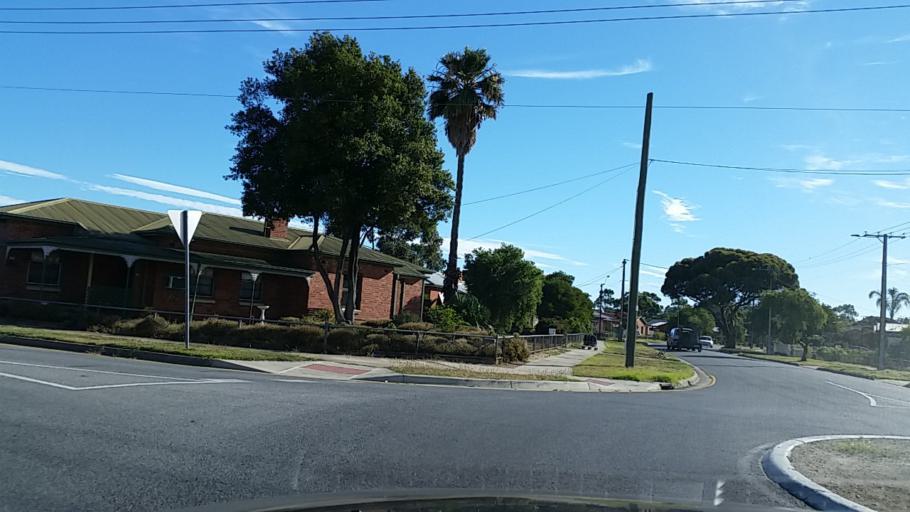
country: AU
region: South Australia
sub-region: Charles Sturt
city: Royal Park
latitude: -34.8828
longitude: 138.5087
